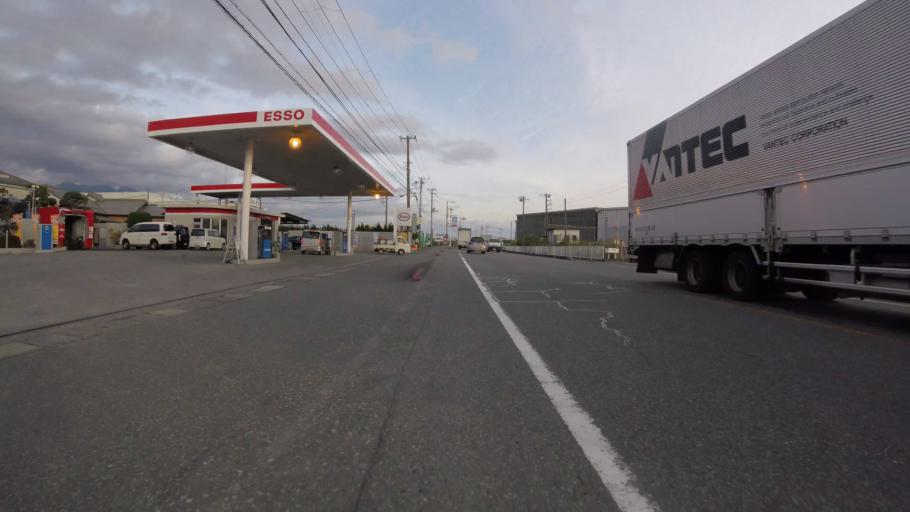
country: JP
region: Shizuoka
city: Fuji
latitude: 35.1469
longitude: 138.7151
